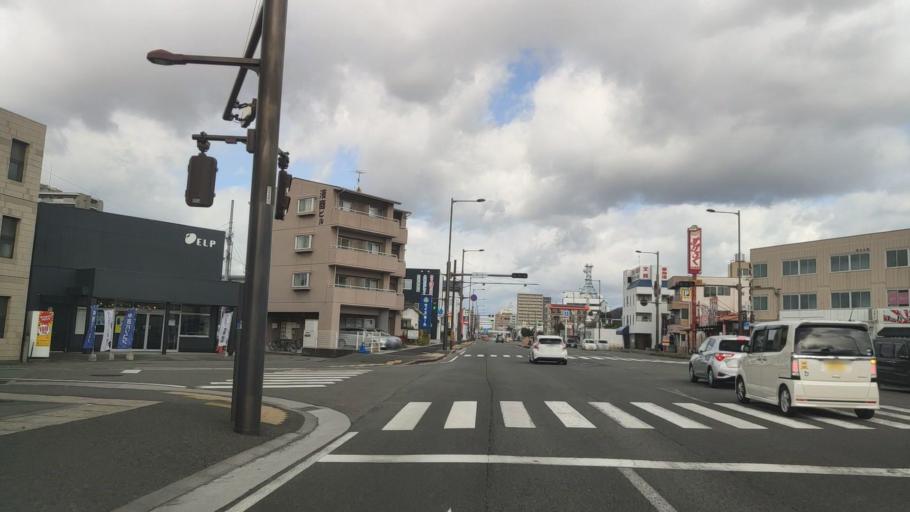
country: JP
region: Ehime
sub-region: Shikoku-chuo Shi
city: Matsuyama
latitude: 33.8277
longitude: 132.7588
